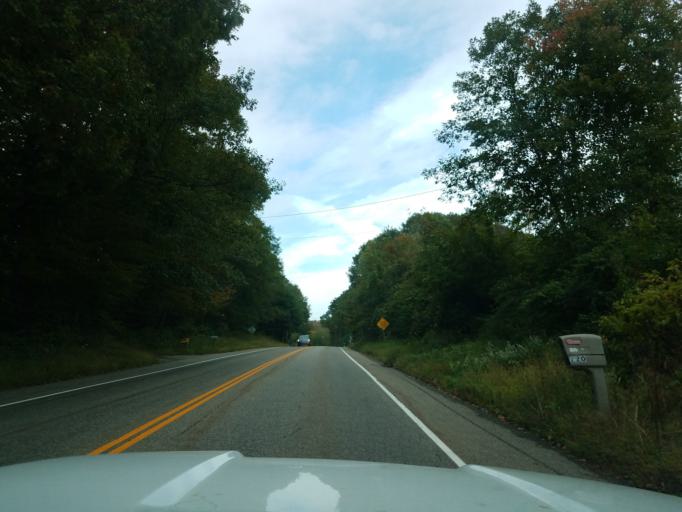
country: US
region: Connecticut
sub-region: Tolland County
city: Hebron
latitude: 41.6638
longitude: -72.3482
